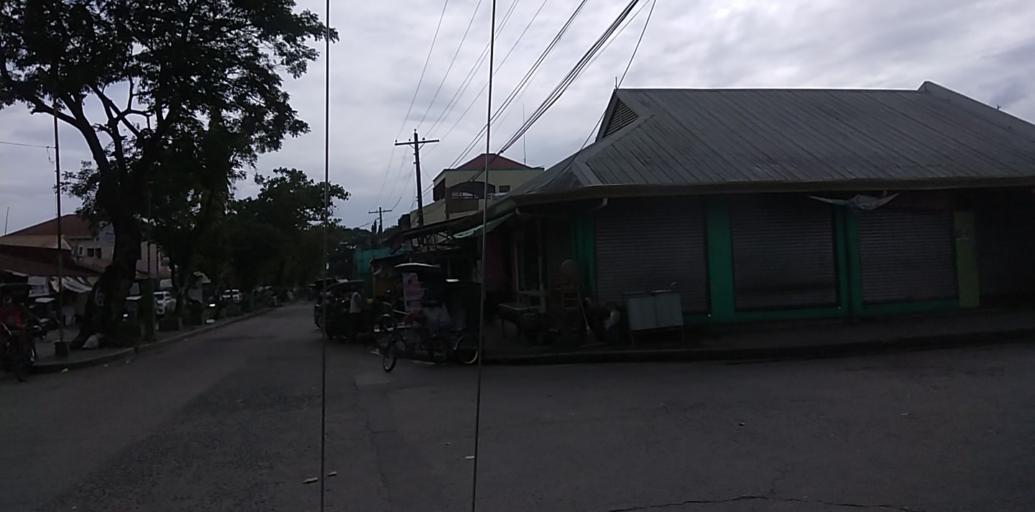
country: PH
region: Central Luzon
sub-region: Province of Pampanga
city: Pio
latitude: 15.0464
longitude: 120.5280
